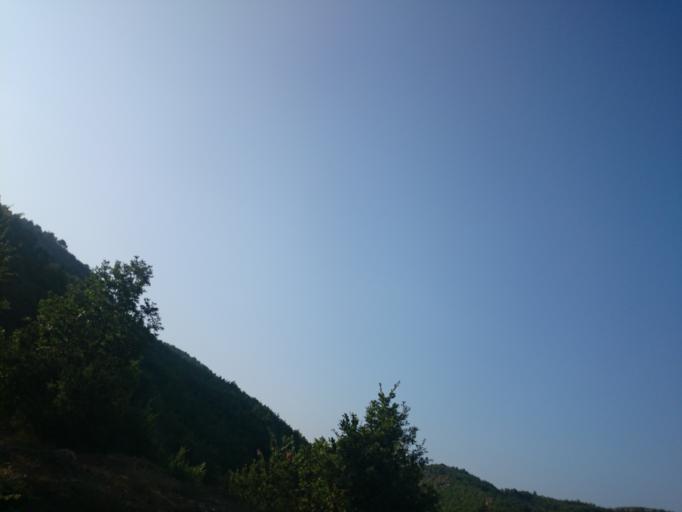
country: AL
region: Diber
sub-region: Rrethi i Dibres
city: Tomin
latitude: 41.6533
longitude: 20.3928
